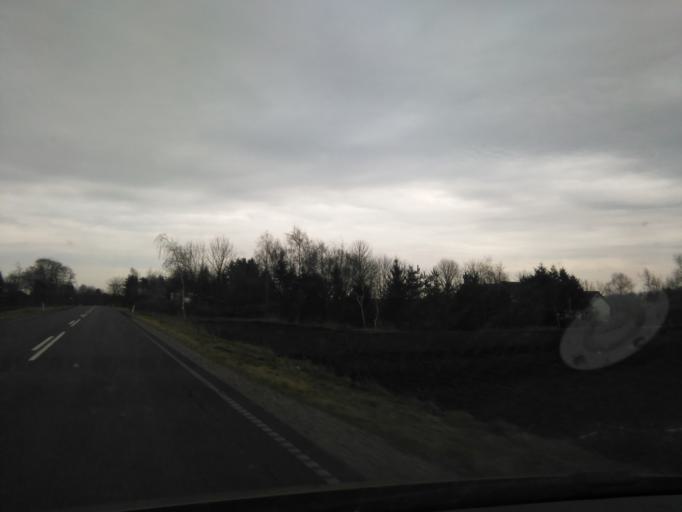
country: DK
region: North Denmark
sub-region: Mariagerfjord Kommune
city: Mariager
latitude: 56.6902
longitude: 9.9581
